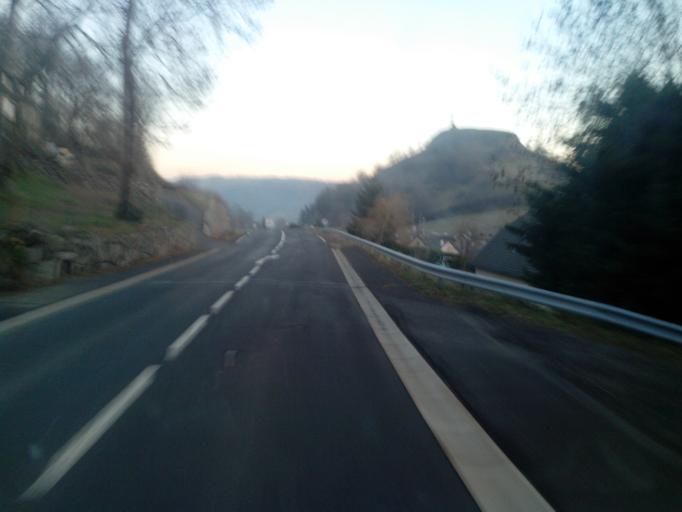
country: FR
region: Auvergne
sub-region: Departement du Cantal
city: Murat
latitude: 45.1162
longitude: 2.8600
